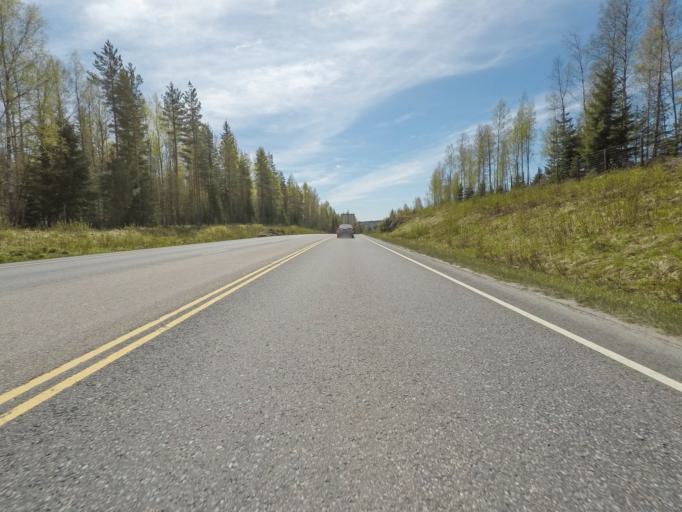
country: FI
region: Pirkanmaa
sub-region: Etelae-Pirkanmaa
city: Urjala
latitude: 61.0352
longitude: 23.5015
